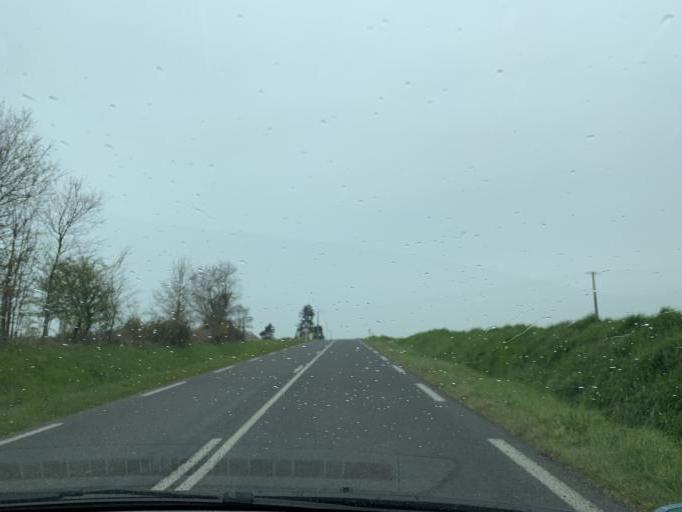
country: FR
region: Haute-Normandie
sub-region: Departement de la Seine-Maritime
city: Cany-Barville
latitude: 49.8090
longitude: 0.6682
